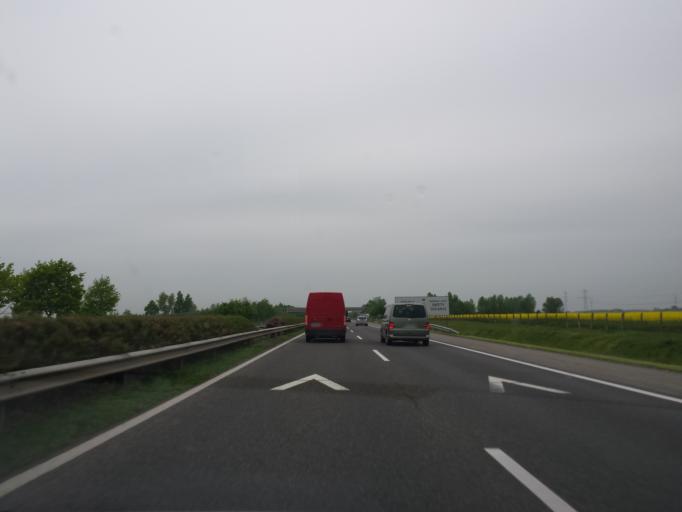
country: HU
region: Gyor-Moson-Sopron
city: Mosonszentmiklos
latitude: 47.7343
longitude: 17.4413
